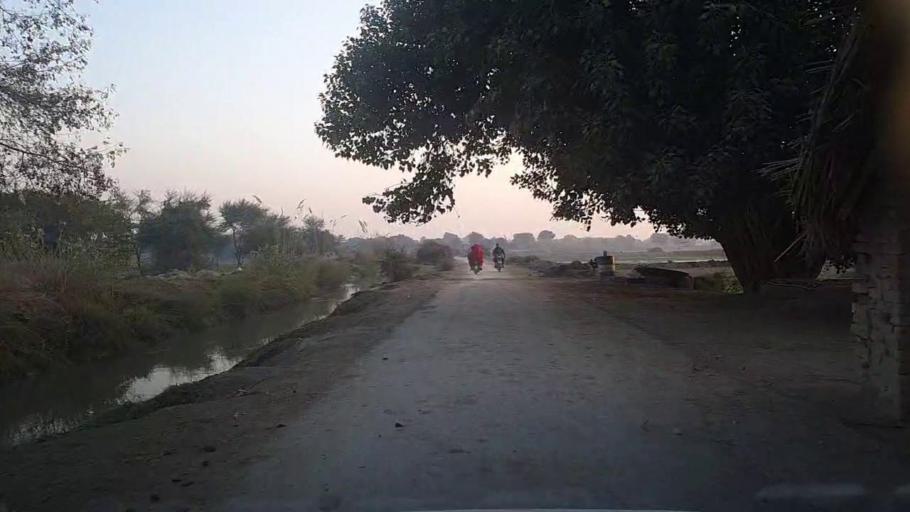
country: PK
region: Sindh
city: Karaundi
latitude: 26.8379
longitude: 68.3694
